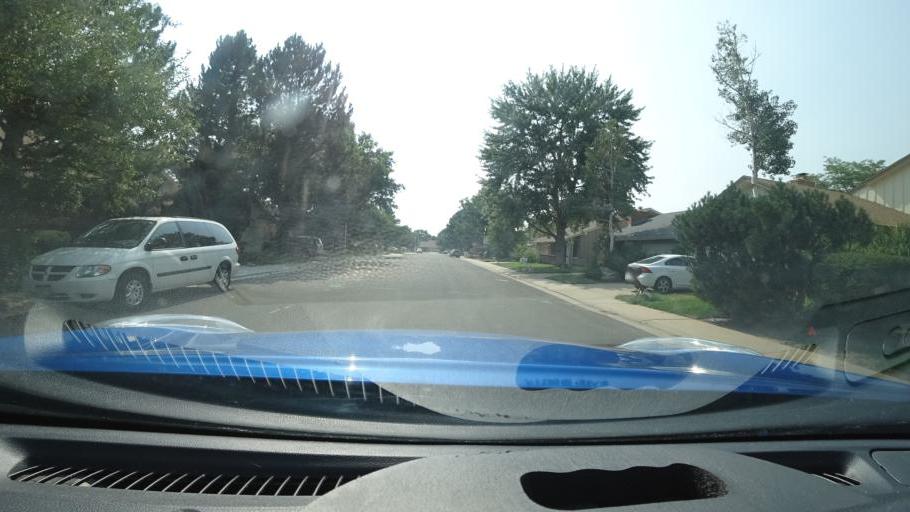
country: US
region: Colorado
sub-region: Adams County
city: Aurora
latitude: 39.6671
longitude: -104.8443
